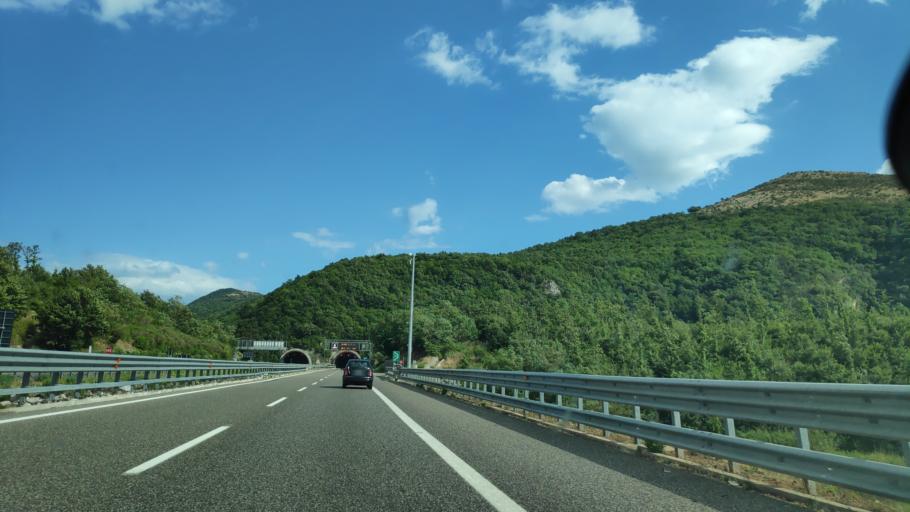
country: IT
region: Campania
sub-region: Provincia di Salerno
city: Sicignano degli Alburni
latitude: 40.6073
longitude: 15.2981
